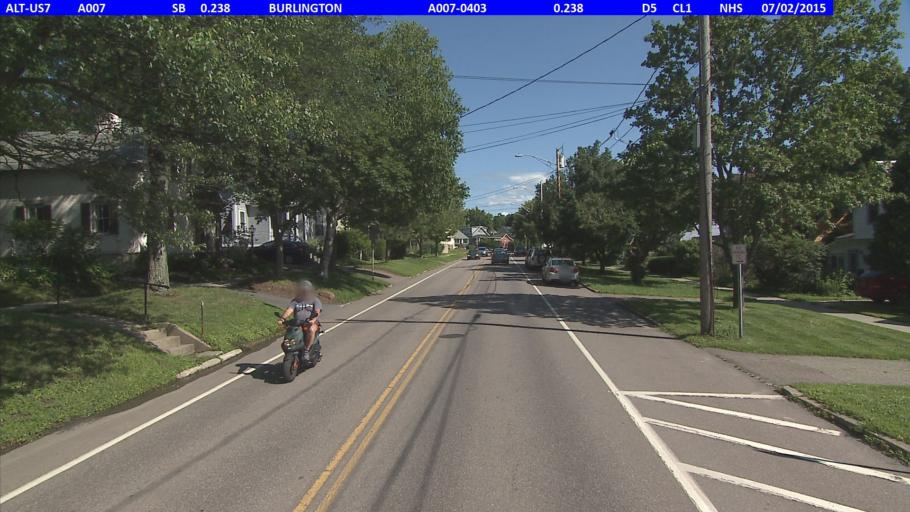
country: US
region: Vermont
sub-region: Chittenden County
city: Burlington
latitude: 44.4663
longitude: -73.2088
